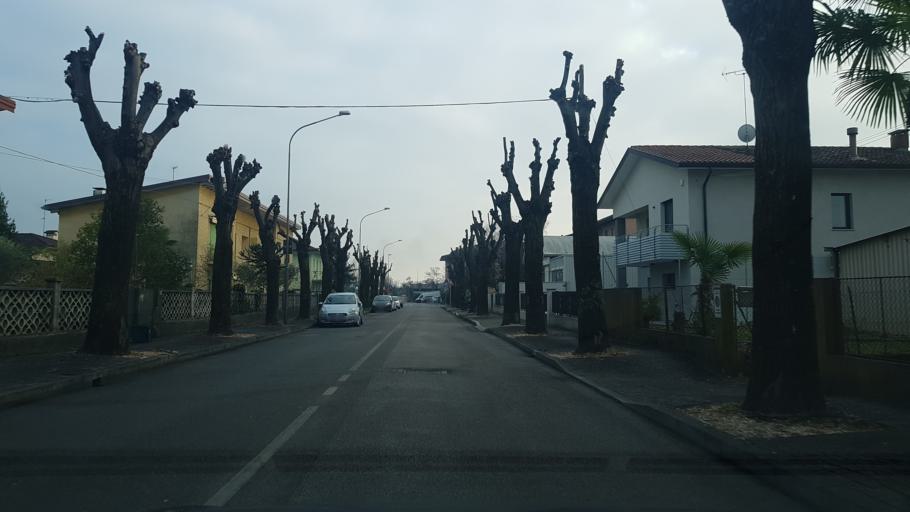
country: IT
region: Friuli Venezia Giulia
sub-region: Provincia di Udine
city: San Giovanni al Natisone
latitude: 45.9771
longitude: 13.4002
